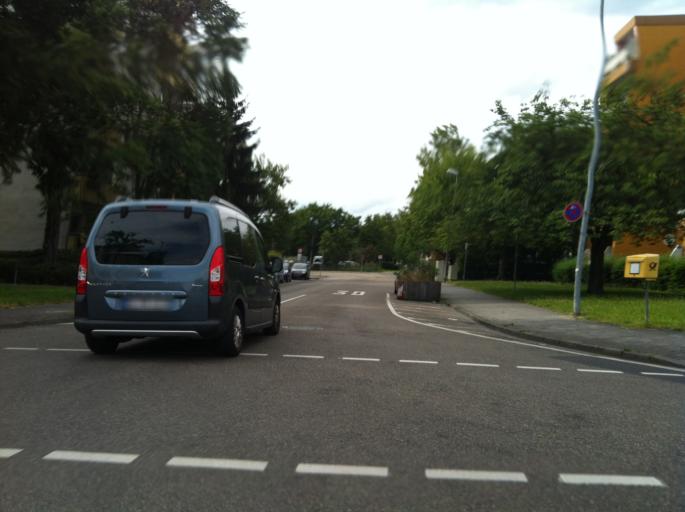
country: DE
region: Rheinland-Pfalz
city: Budenheim
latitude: 50.0083
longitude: 8.2118
